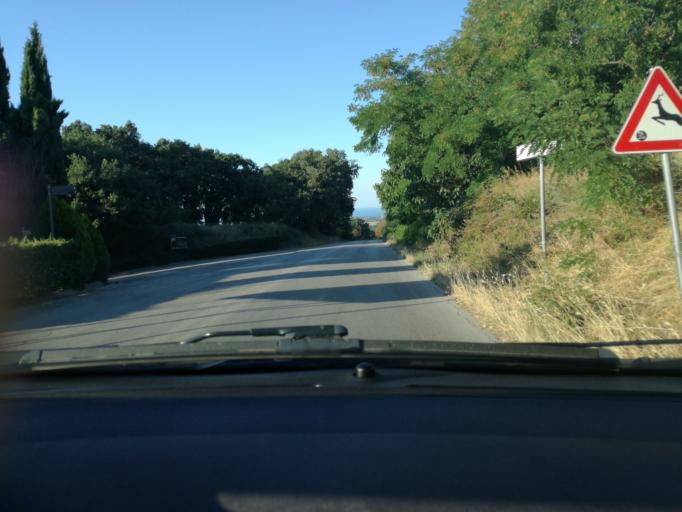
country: IT
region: Molise
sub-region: Provincia di Campobasso
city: Guglionesi
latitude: 41.9272
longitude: 14.9250
